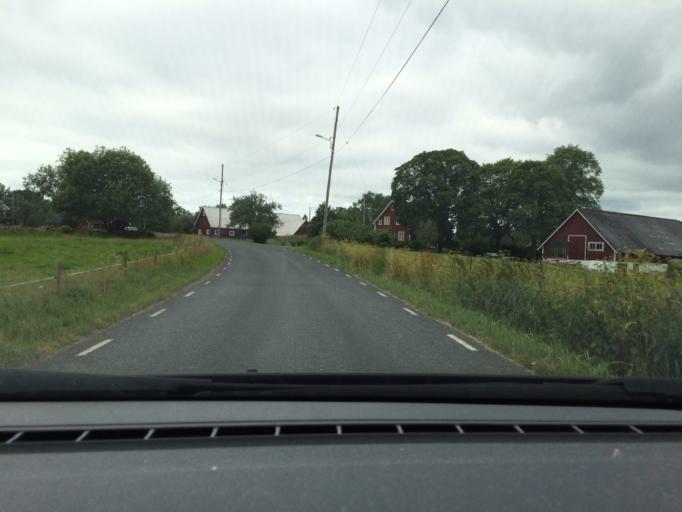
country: SE
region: Joenkoeping
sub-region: Varnamo Kommun
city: Forsheda
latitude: 57.0770
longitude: 13.8076
